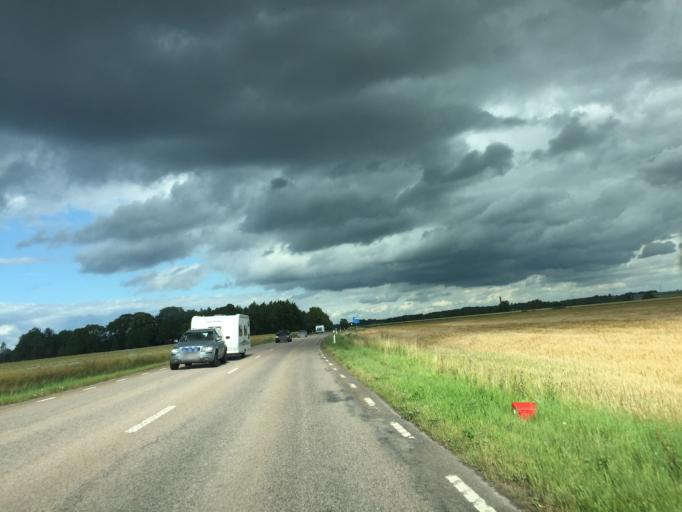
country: SE
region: OEstergoetland
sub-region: Vadstena Kommun
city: Vadstena
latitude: 58.4549
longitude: 14.9142
